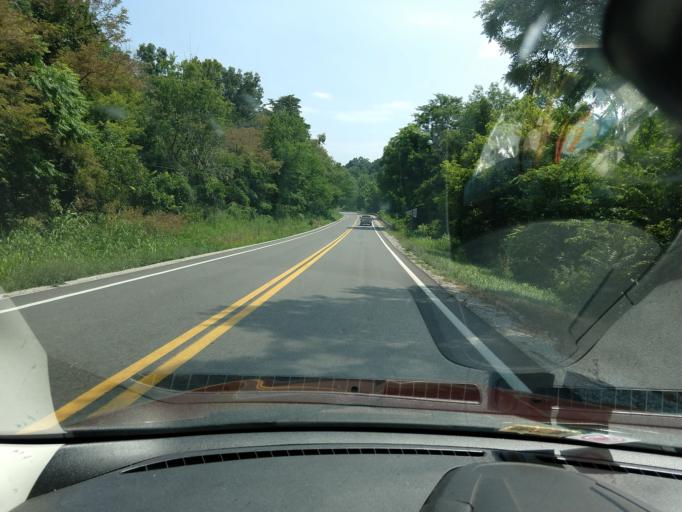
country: US
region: West Virginia
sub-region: Jackson County
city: Ravenswood
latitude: 38.8690
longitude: -81.8774
